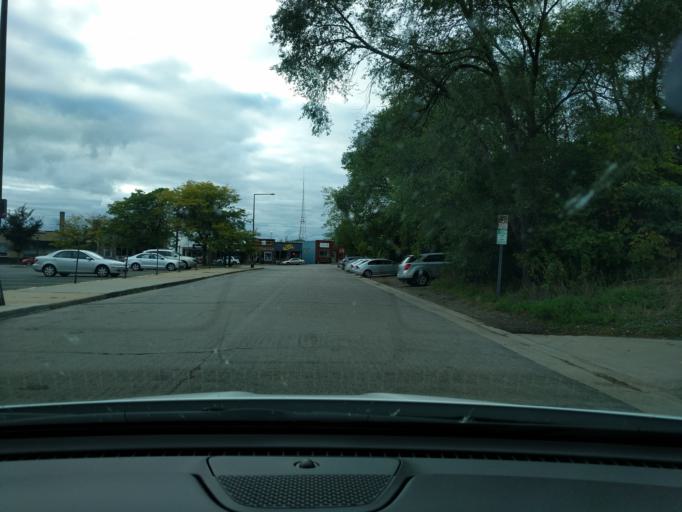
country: US
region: Minnesota
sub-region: Ramsey County
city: Lauderdale
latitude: 44.9648
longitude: -93.1965
